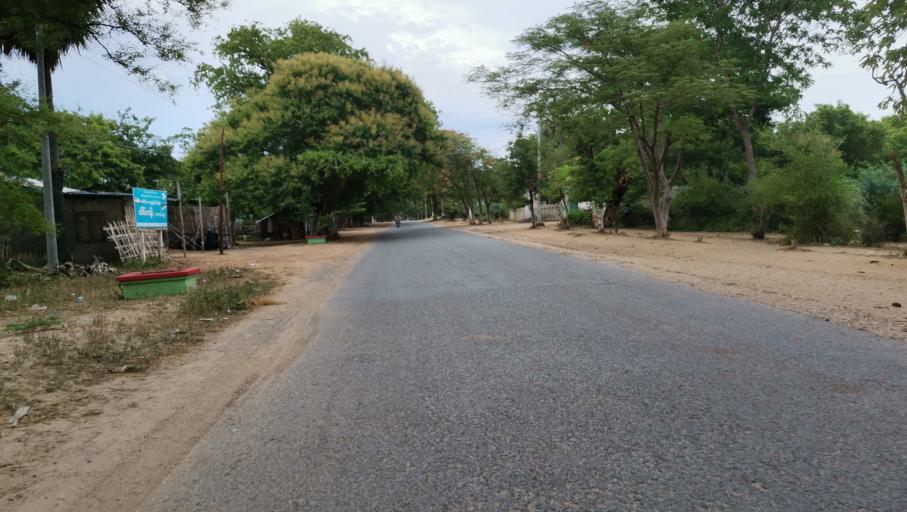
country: MM
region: Mandalay
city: Myingyan
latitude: 21.8441
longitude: 95.4277
